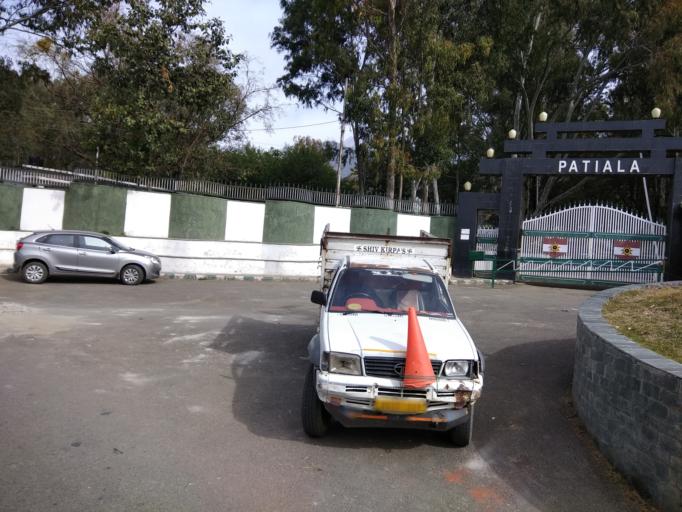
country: IN
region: Himachal Pradesh
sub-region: Kangra
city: Dharmsala
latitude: 32.1790
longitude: 76.3788
